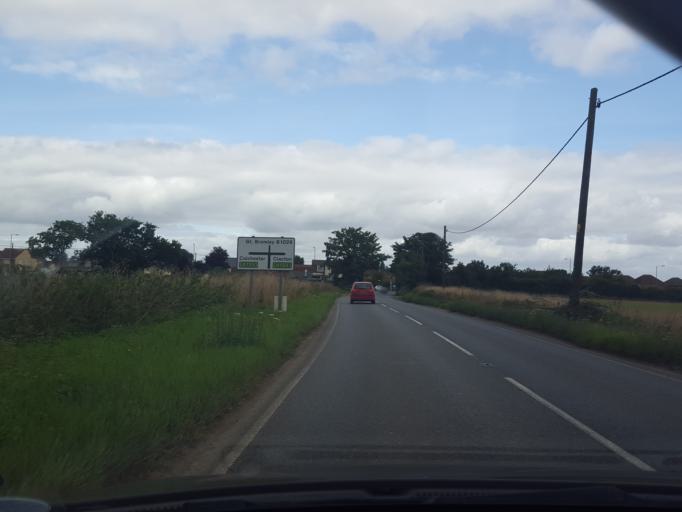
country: GB
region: England
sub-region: Essex
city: Great Bentley
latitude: 51.8674
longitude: 1.0369
